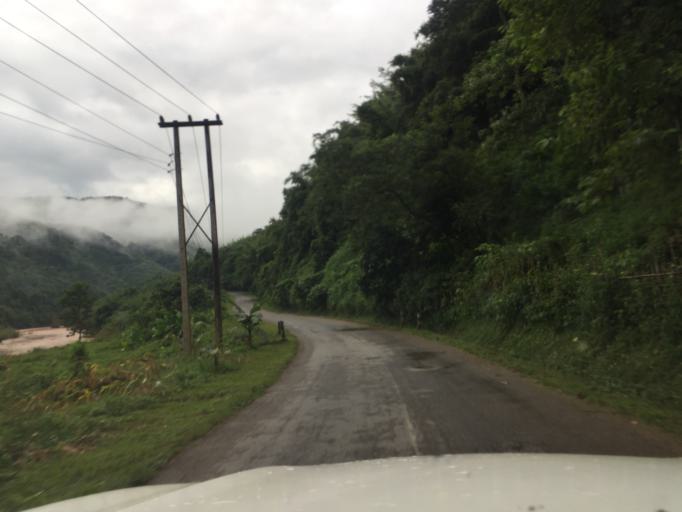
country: LA
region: Oudomxai
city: Muang La
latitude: 20.9050
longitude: 102.1799
